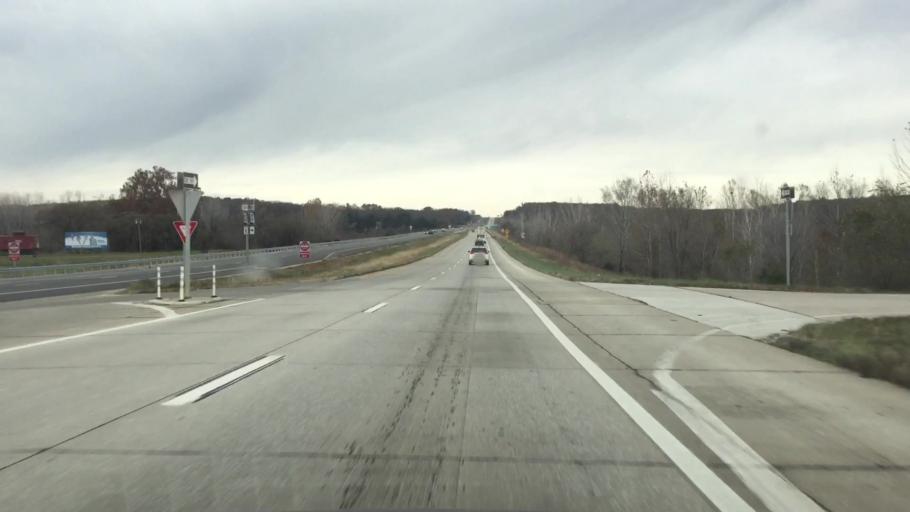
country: US
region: Missouri
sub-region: Saint Clair County
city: Osceola
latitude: 38.0537
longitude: -93.6889
